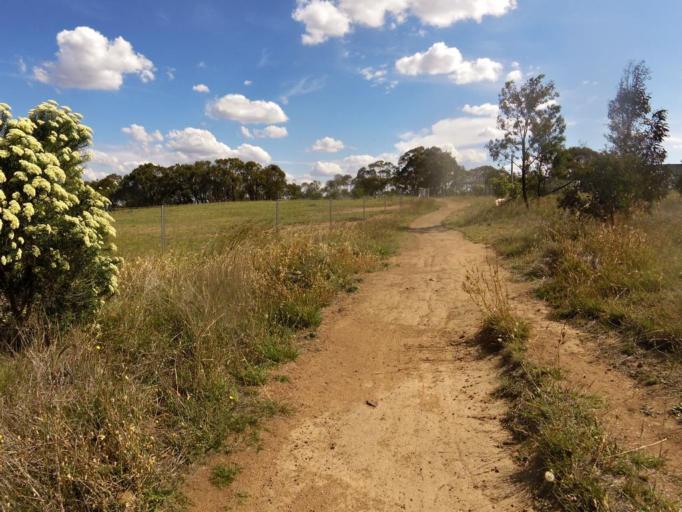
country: AU
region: Australian Capital Territory
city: Belconnen
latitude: -35.1642
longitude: 149.0730
